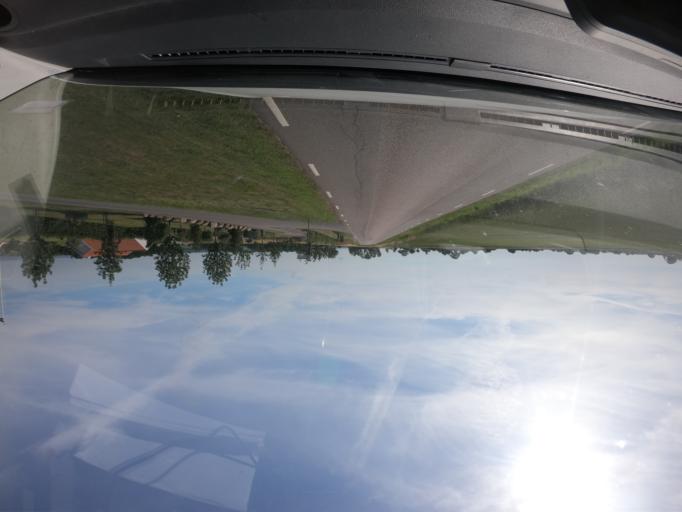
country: SE
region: Skane
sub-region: Bastads Kommun
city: Forslov
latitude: 56.3669
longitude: 12.7736
